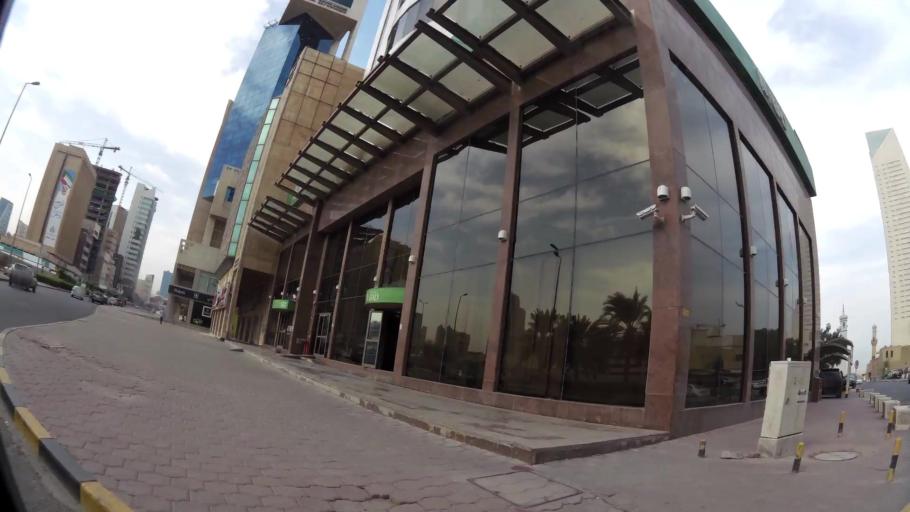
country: KW
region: Al Asimah
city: Kuwait City
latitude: 29.3789
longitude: 47.9802
